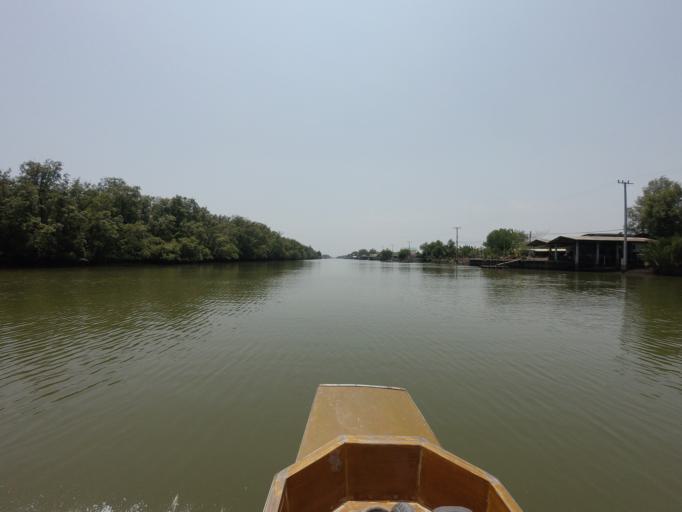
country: TH
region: Bangkok
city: Thung Khru
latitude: 13.5449
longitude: 100.4796
